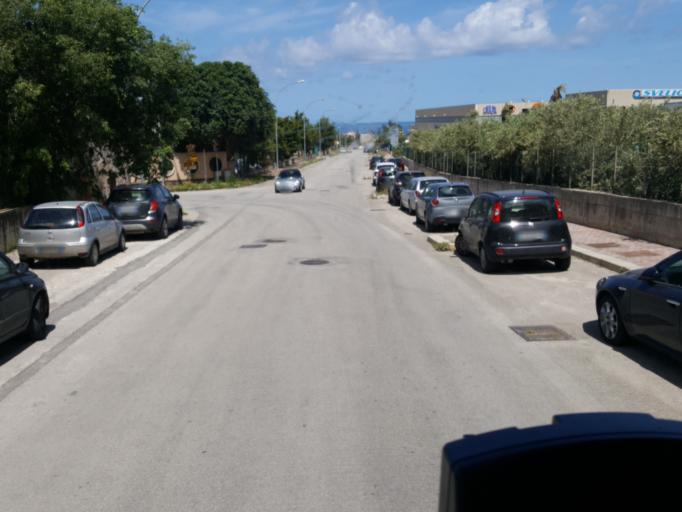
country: IT
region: Sicily
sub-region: Palermo
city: Carini
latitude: 38.1541
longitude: 13.2114
